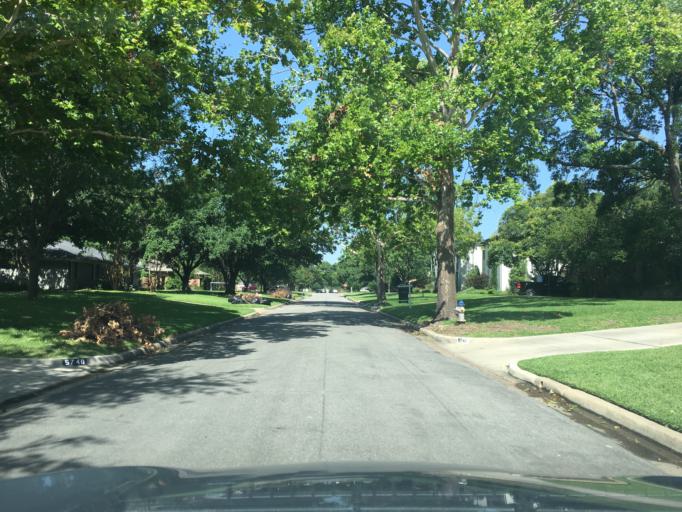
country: US
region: Texas
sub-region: Dallas County
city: University Park
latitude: 32.9066
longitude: -96.8088
